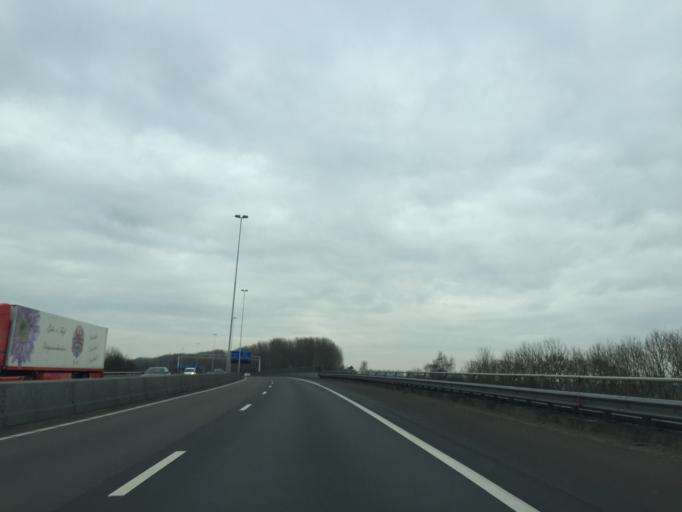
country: NL
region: South Holland
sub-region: Gemeente Giessenlanden
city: Giessenburg
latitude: 51.8391
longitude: 4.9278
